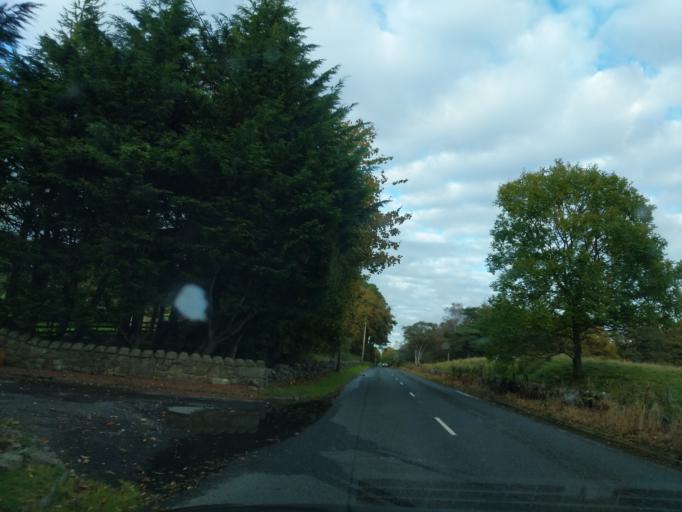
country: GB
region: Scotland
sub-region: Midlothian
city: Penicuik
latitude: 55.8159
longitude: -3.2809
